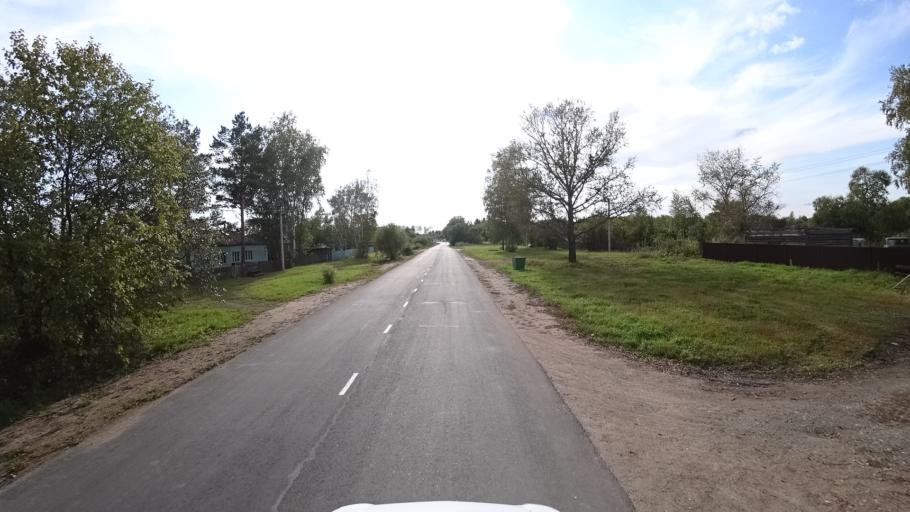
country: RU
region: Amur
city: Arkhara
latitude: 49.3659
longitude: 130.1281
